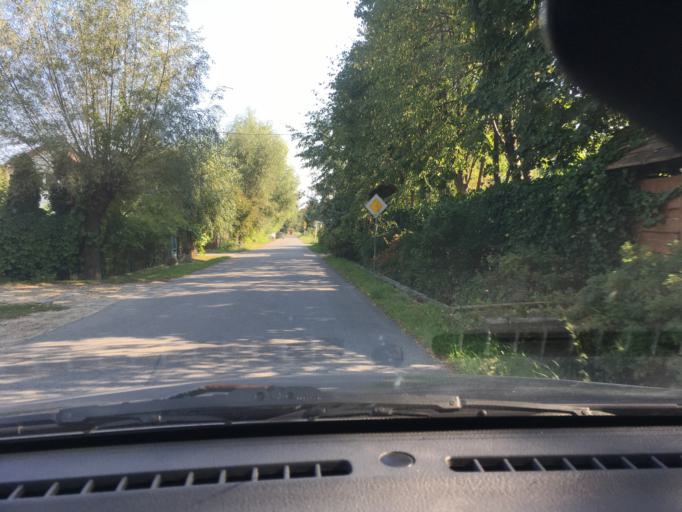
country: PL
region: Masovian Voivodeship
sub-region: Powiat piaseczynski
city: Lesznowola
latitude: 52.0532
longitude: 20.9430
